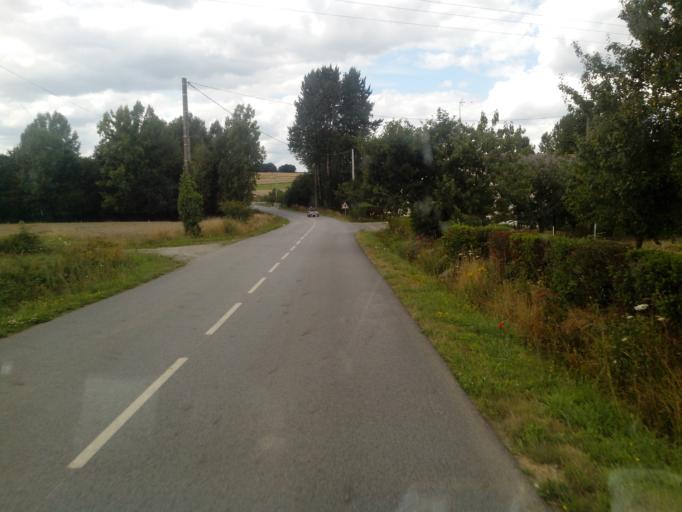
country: FR
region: Brittany
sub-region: Departement du Morbihan
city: Guilliers
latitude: 48.0688
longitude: -2.4239
